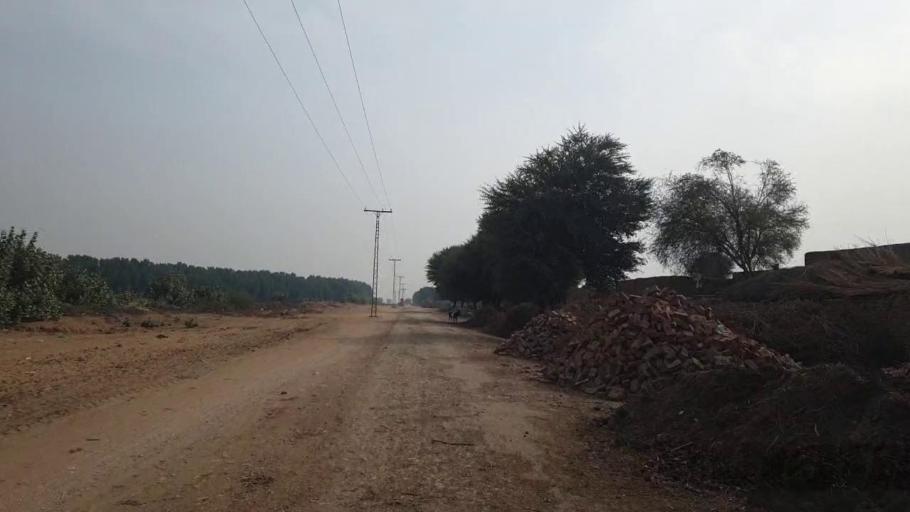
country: PK
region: Sindh
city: Sann
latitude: 26.0311
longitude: 68.1367
